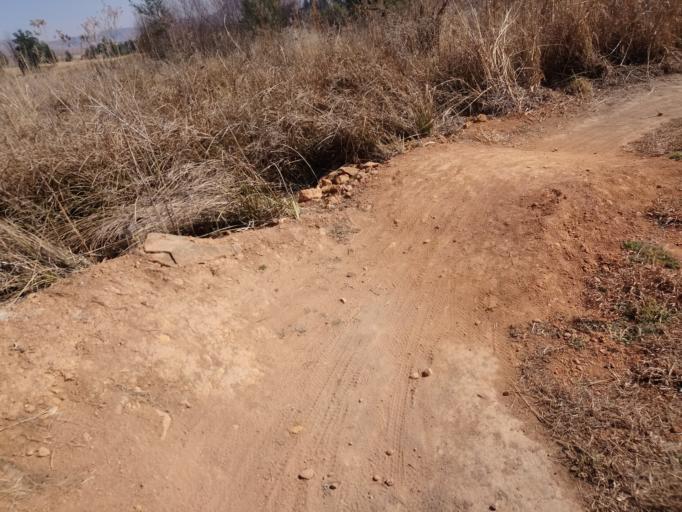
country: ZA
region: KwaZulu-Natal
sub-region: uMgungundlovu District Municipality
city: Mooirivier
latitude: -29.3231
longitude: 29.7141
